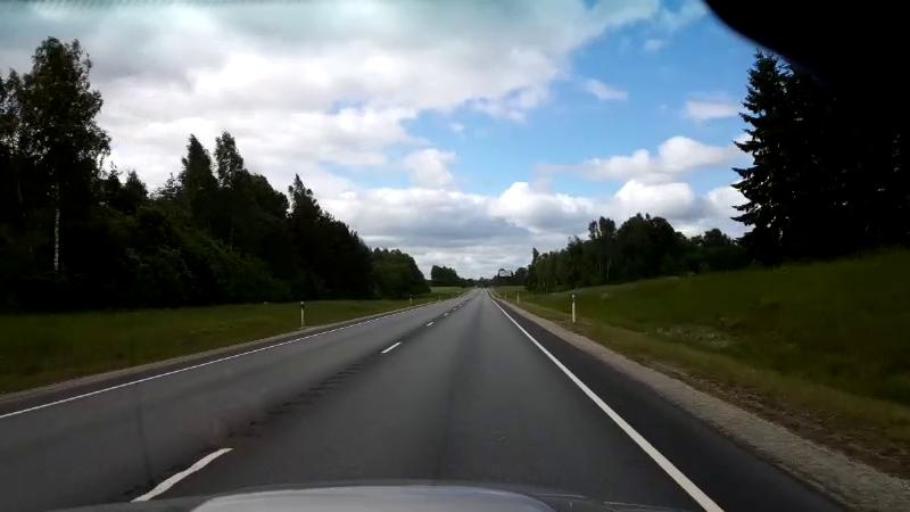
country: EE
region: Harju
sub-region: Nissi vald
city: Riisipere
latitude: 59.0863
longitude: 24.4604
